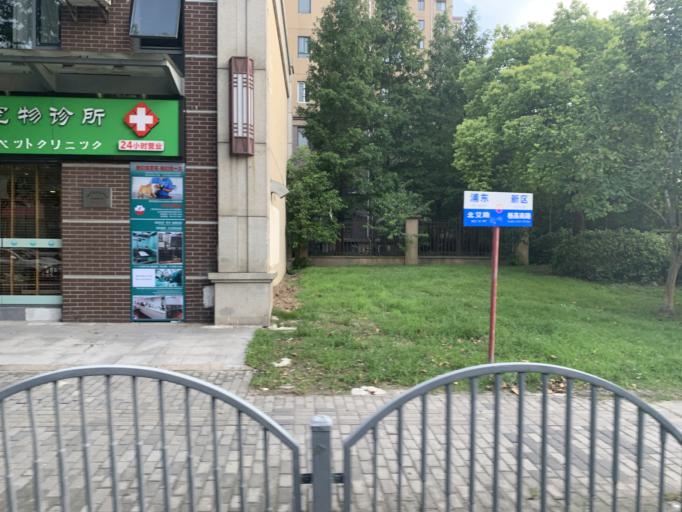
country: CN
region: Shanghai Shi
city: Huamu
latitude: 31.1814
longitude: 121.5170
